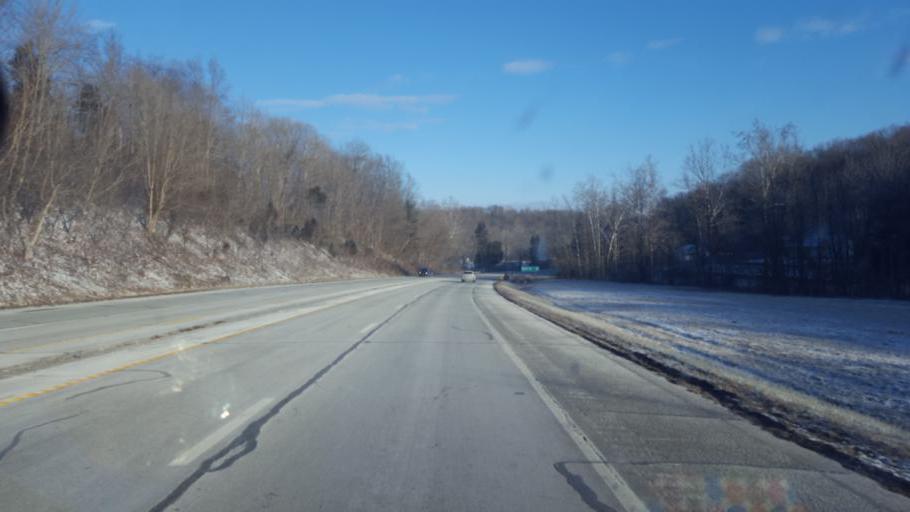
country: US
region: Ohio
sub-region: Pike County
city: Waverly
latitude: 39.1730
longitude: -82.9756
